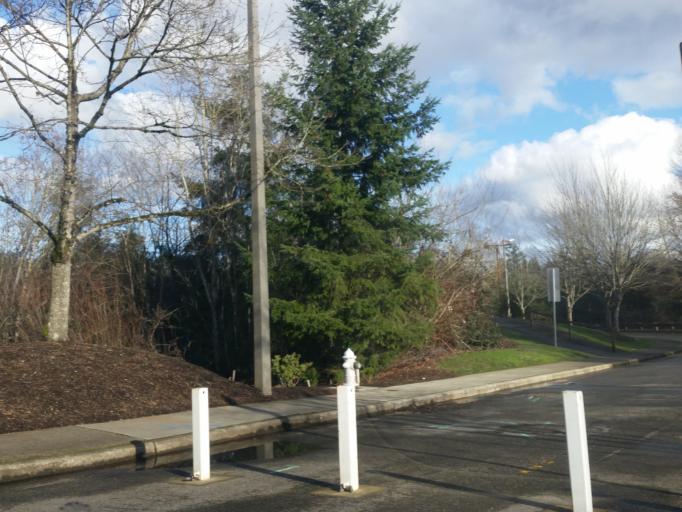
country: US
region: Washington
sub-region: King County
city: Bothell
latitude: 47.7584
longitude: -122.2073
